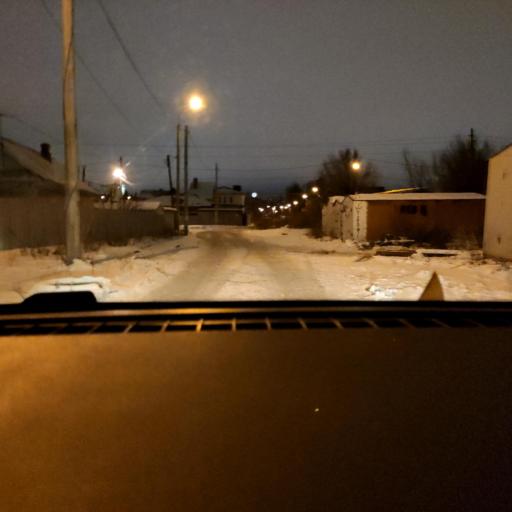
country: RU
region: Samara
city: Samara
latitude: 53.1846
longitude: 50.2134
